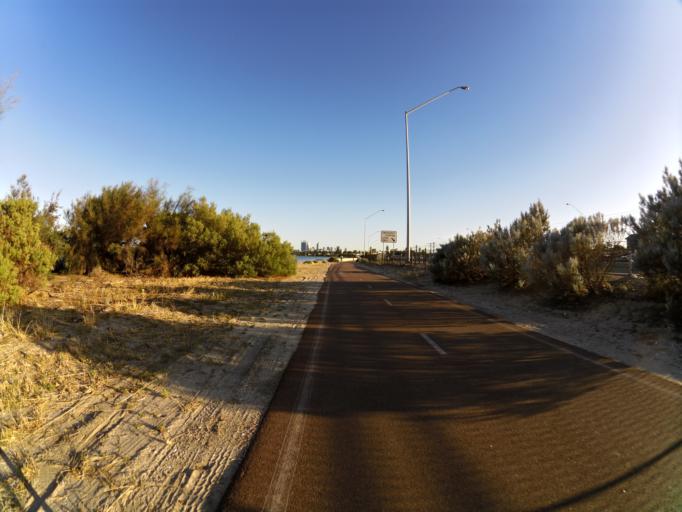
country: AU
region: Western Australia
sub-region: South Perth
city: Como
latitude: -32.0030
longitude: 115.8534
